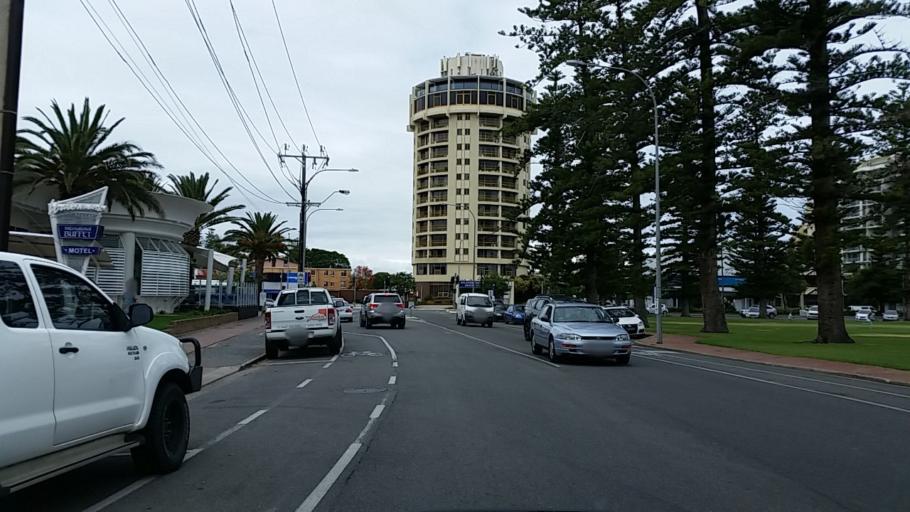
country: AU
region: South Australia
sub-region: Adelaide
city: Glenelg
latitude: -34.9757
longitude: 138.5141
